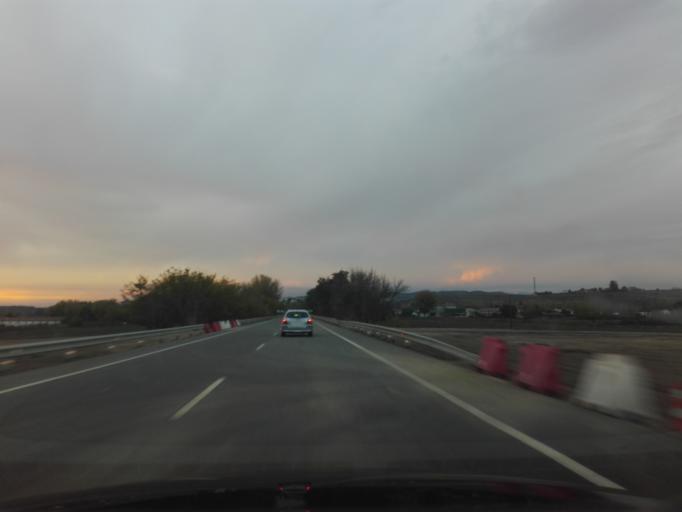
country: ES
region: Extremadura
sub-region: Provincia de Caceres
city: Coria
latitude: 39.9708
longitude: -6.5228
